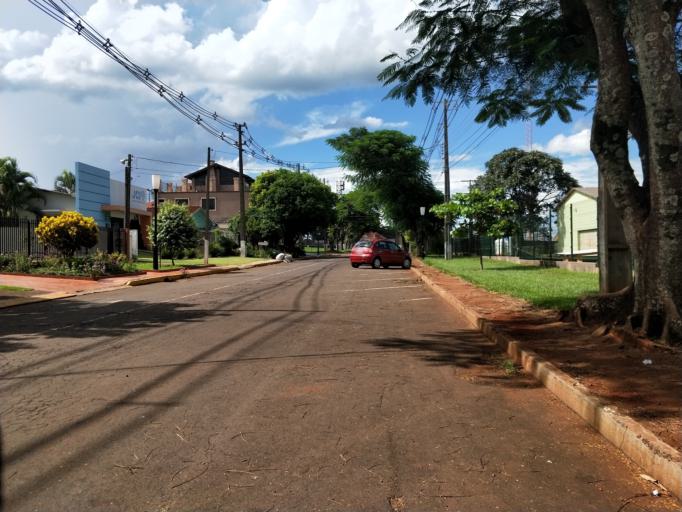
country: BR
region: Parana
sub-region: Marechal Candido Rondon
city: Marechal Candido Rondon
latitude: -24.5565
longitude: -54.0491
